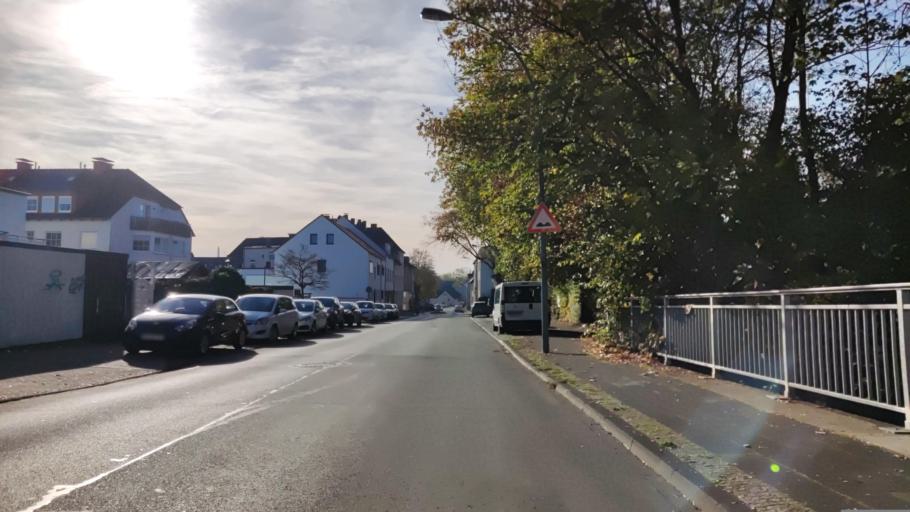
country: DE
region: North Rhine-Westphalia
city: Bochum-Hordel
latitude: 51.5267
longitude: 7.1841
